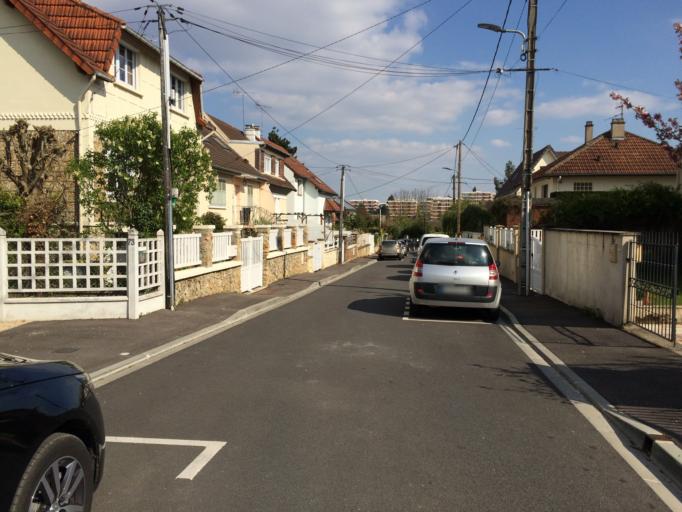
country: FR
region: Ile-de-France
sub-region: Departement des Yvelines
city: Jouy-en-Josas
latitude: 48.7571
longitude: 2.1813
